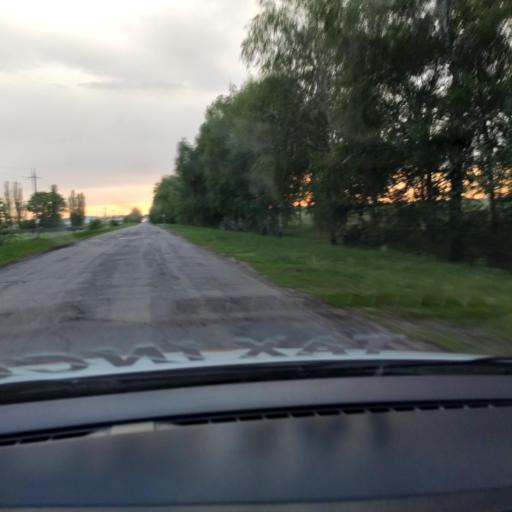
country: RU
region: Voronezj
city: Maslovka
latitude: 51.4428
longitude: 39.2676
